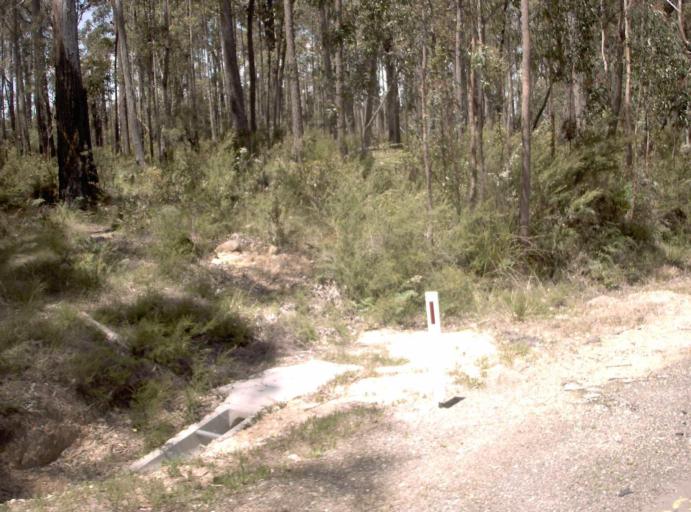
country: AU
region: Victoria
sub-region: East Gippsland
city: Lakes Entrance
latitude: -37.6983
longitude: 148.6402
